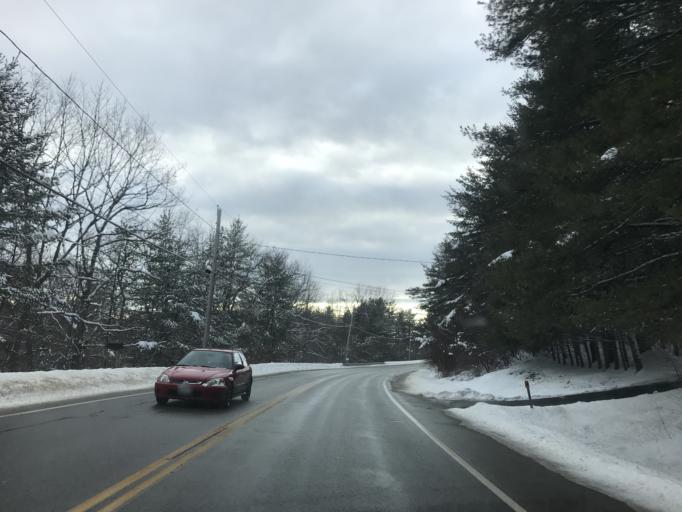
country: US
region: Maine
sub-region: Cumberland County
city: Westbrook
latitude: 43.7005
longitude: -70.3281
